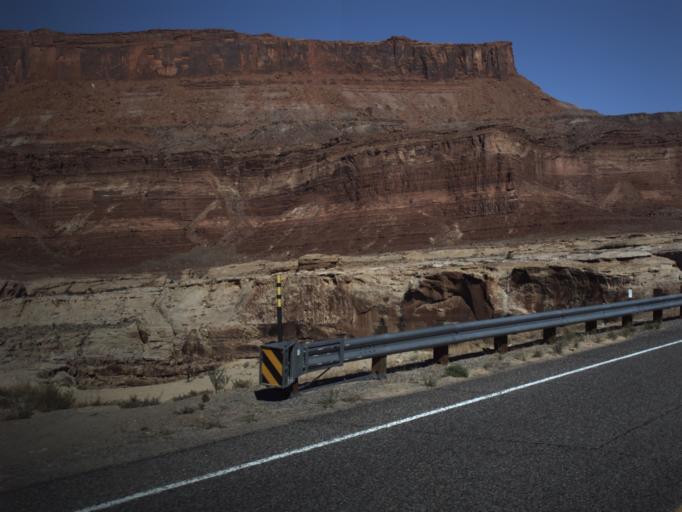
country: US
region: Utah
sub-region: San Juan County
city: Blanding
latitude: 37.9145
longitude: -110.3880
